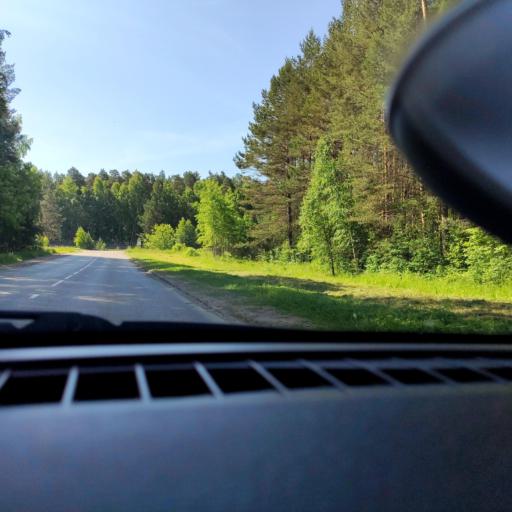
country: RU
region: Perm
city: Overyata
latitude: 57.9952
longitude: 55.8823
